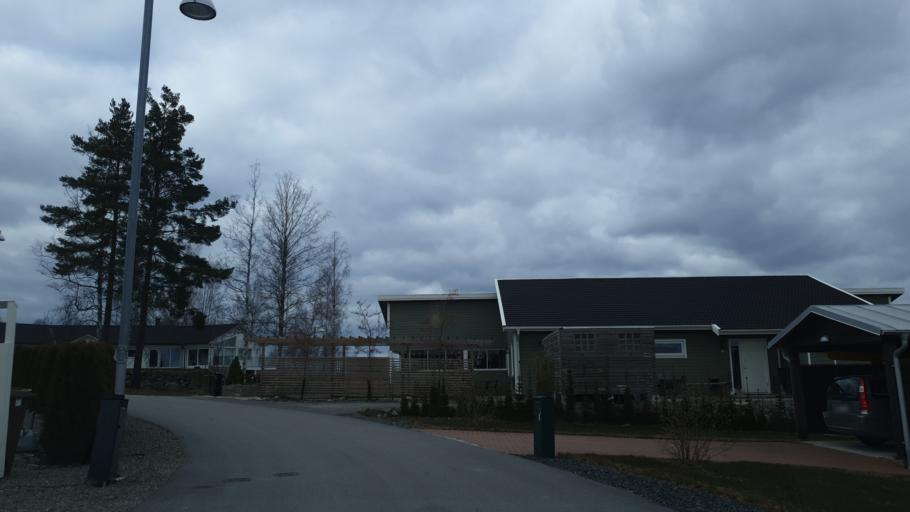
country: SE
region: OErebro
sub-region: Nora Kommun
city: Nora
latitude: 59.5310
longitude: 15.0426
